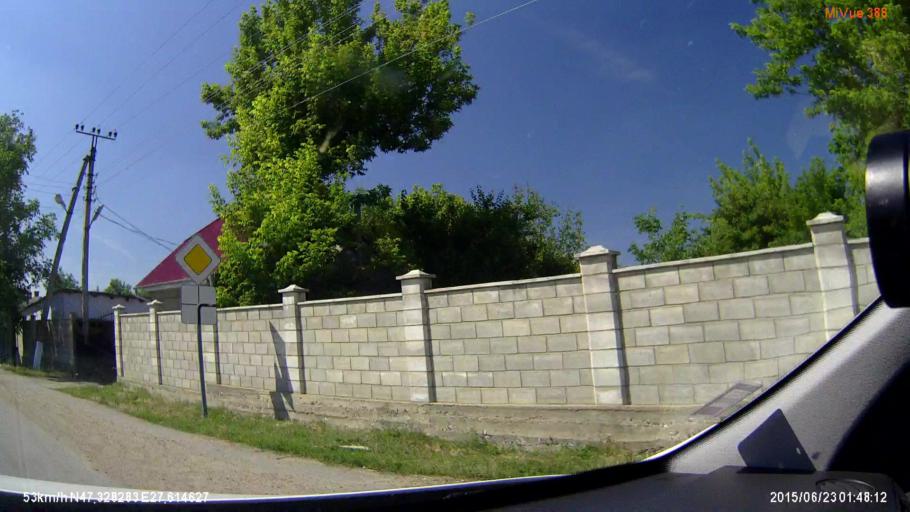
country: RO
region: Iasi
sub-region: Comuna Victoria
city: Victoria
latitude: 47.3282
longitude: 27.6148
